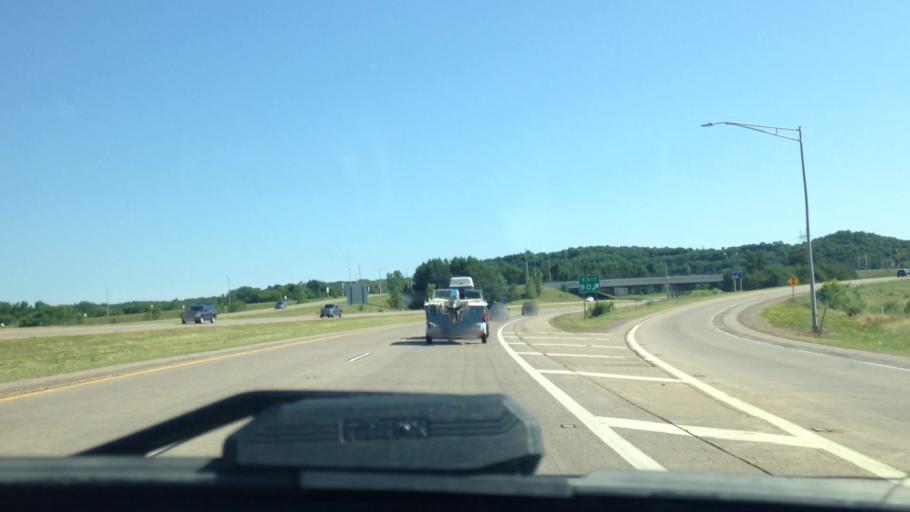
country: US
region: Wisconsin
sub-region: Eau Claire County
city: Seymour
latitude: 44.8316
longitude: -91.4533
